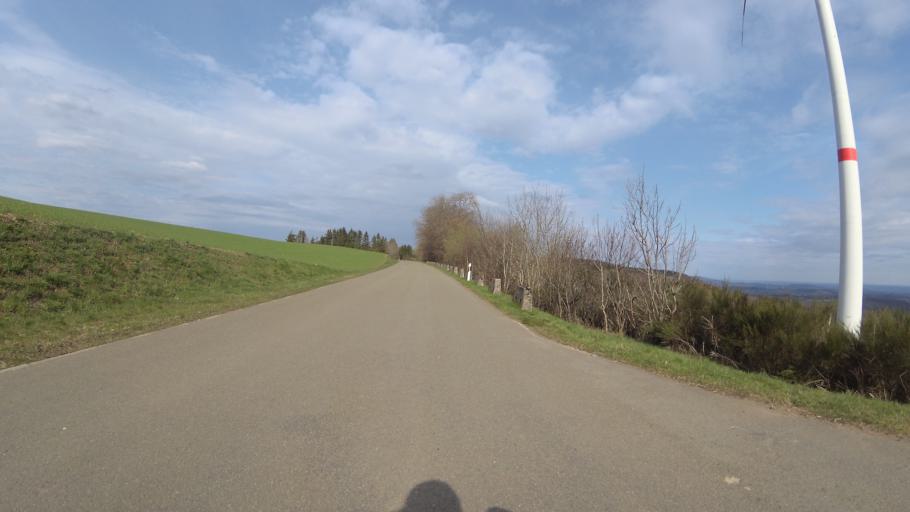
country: DE
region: Rheinland-Pfalz
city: Eckersweiler
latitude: 49.5522
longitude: 7.2822
